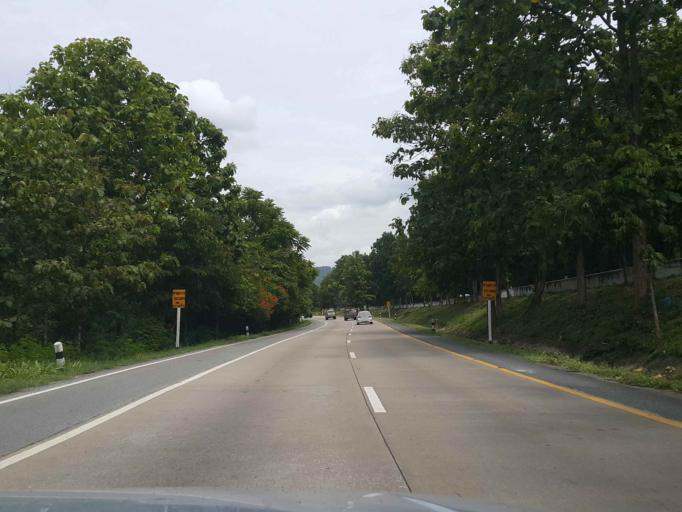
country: TH
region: Lamphun
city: Mae Tha
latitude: 18.4615
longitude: 99.1789
